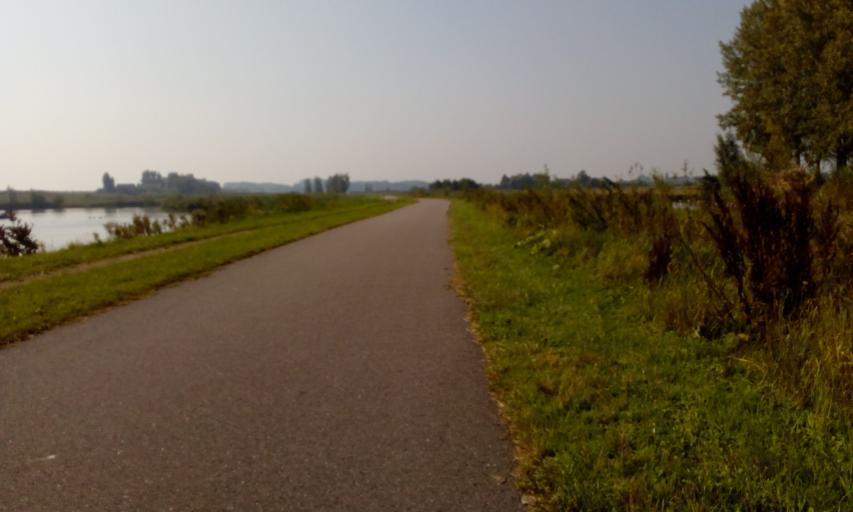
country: NL
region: South Holland
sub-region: Gemeente Lansingerland
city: Bleiswijk
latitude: 52.0268
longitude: 4.5552
